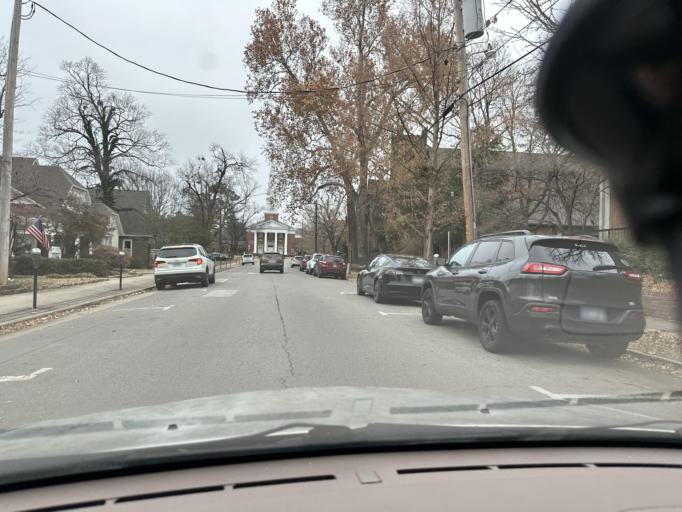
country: US
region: Arkansas
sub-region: Washington County
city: Fayetteville
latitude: 36.0651
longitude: -94.1596
